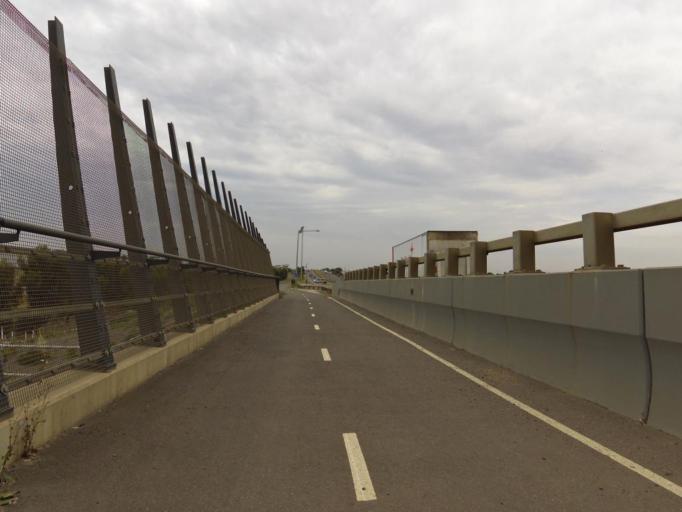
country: AU
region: Victoria
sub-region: Brimbank
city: Derrimut
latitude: -37.7730
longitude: 144.7466
